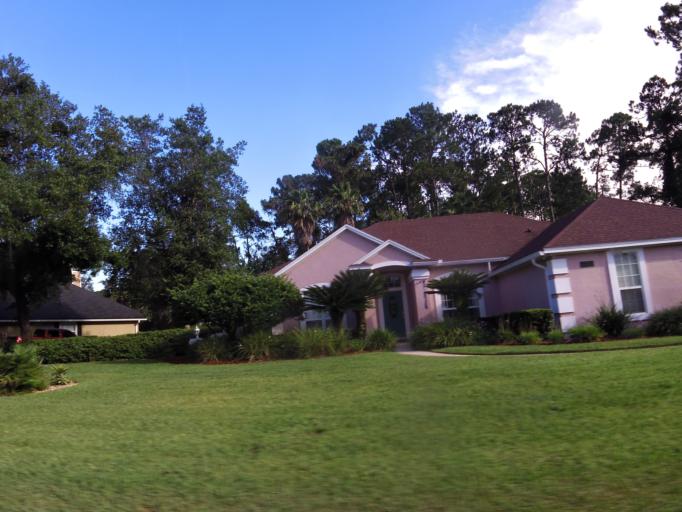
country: US
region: Florida
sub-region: Saint Johns County
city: Fruit Cove
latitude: 30.2097
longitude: -81.5350
